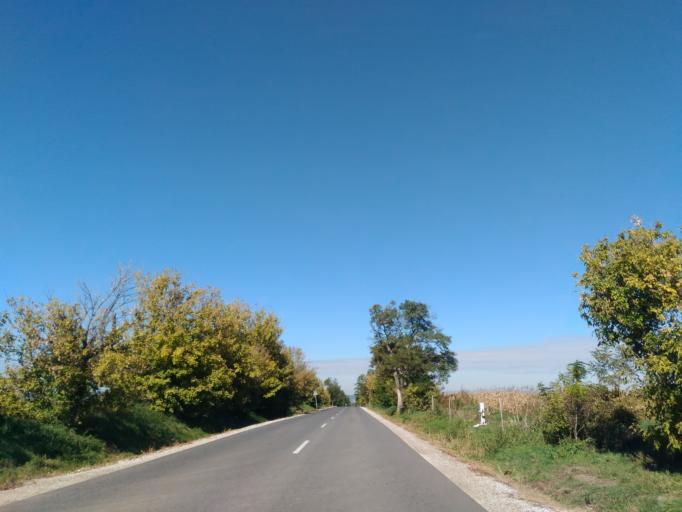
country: HU
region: Fejer
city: Kapolnasnyek
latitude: 47.2045
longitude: 18.6918
